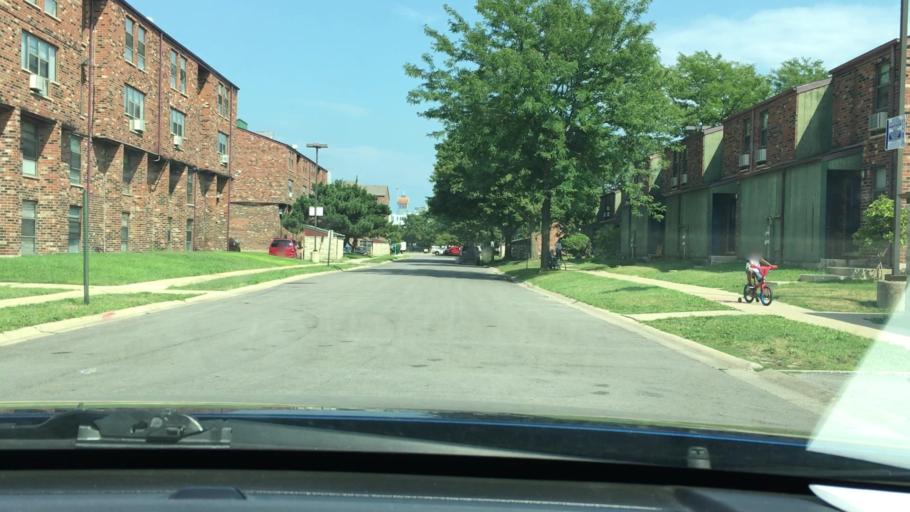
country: US
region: Illinois
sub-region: Cook County
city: Chicago
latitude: 41.8634
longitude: -87.6533
